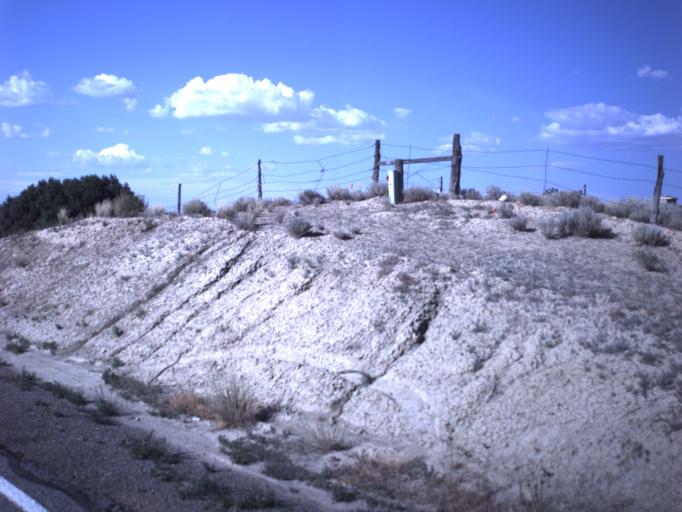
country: US
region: Utah
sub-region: Emery County
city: Huntington
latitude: 39.3948
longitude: -110.8525
